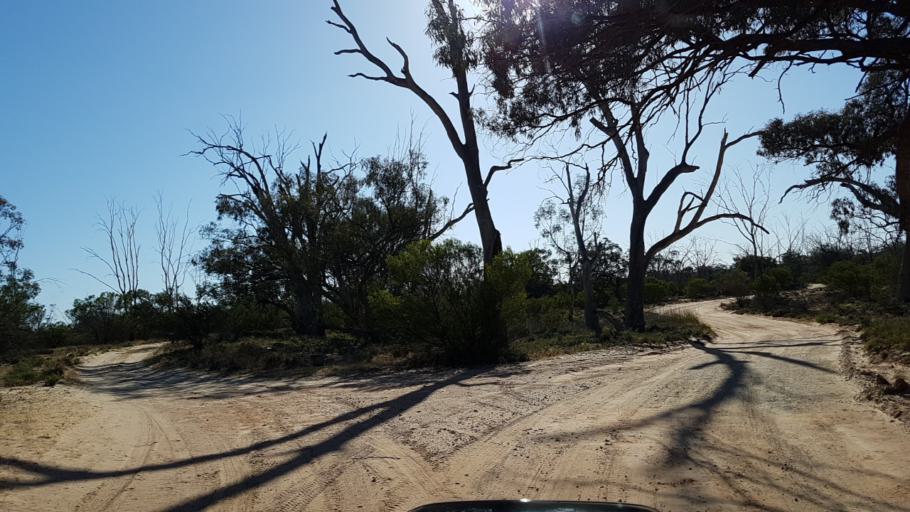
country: AU
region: South Australia
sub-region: Loxton Waikerie
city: Waikerie
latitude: -34.1582
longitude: 140.0262
